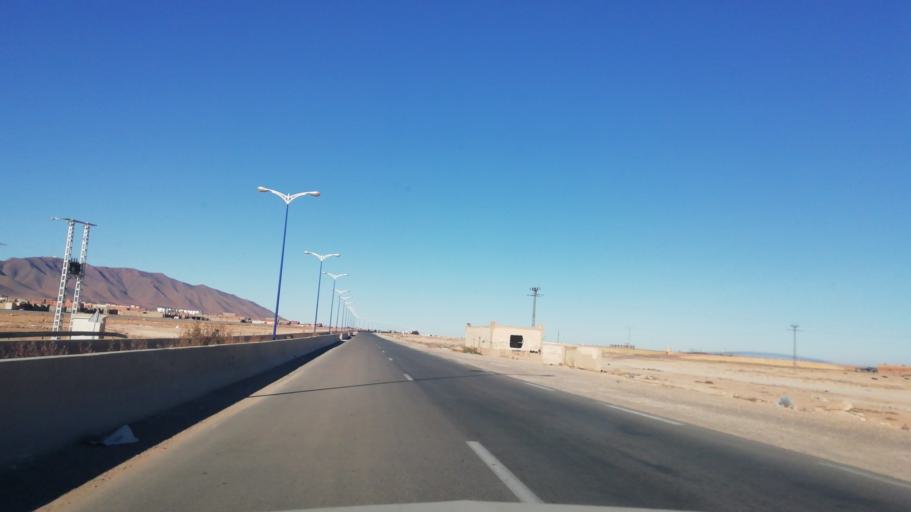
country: DZ
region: Wilaya de Naama
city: Naama
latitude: 33.5149
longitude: -0.2774
